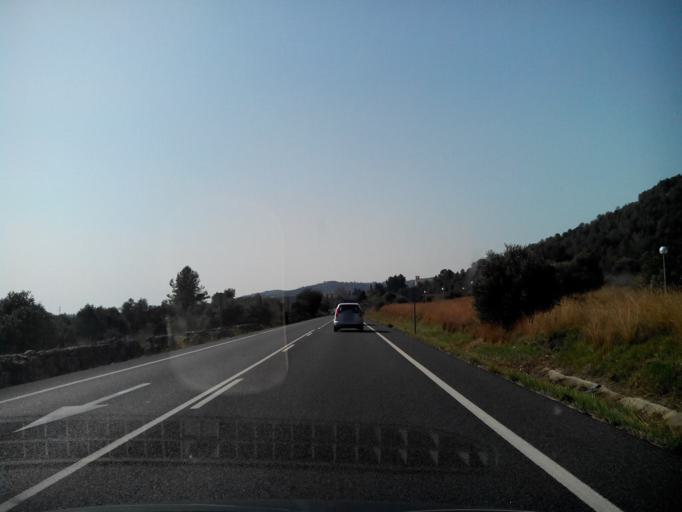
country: ES
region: Catalonia
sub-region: Provincia de Tarragona
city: Alcover
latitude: 41.2739
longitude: 1.1780
